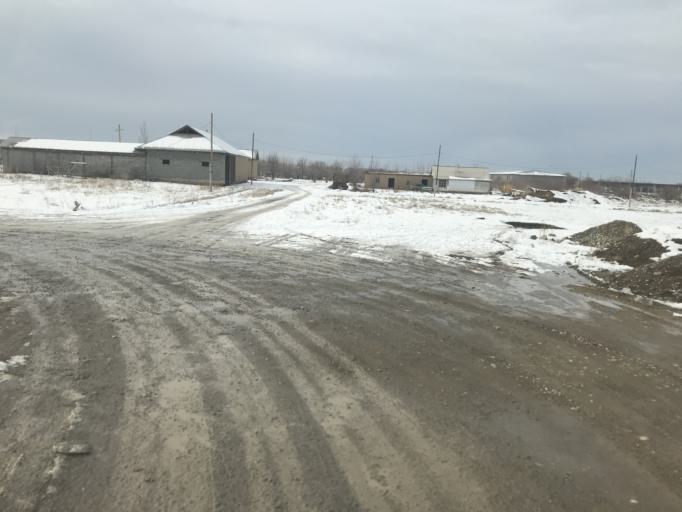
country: KZ
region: Ongtustik Qazaqstan
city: Aksu
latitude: 42.4755
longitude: 69.8182
